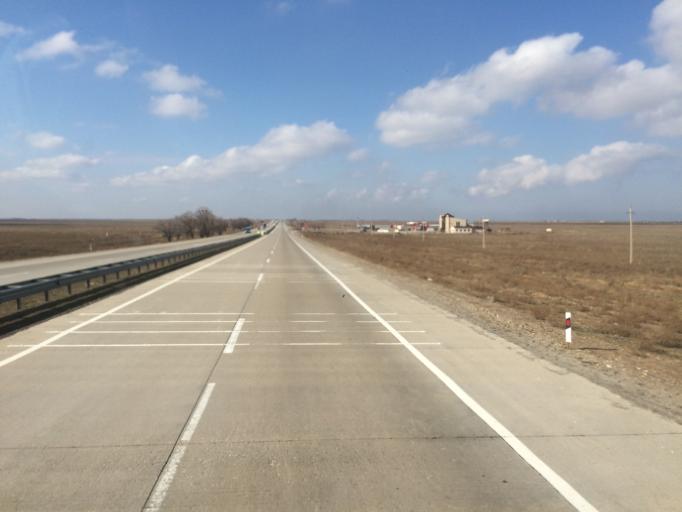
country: KZ
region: Ongtustik Qazaqstan
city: Temirlanovka
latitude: 42.8384
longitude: 69.1110
